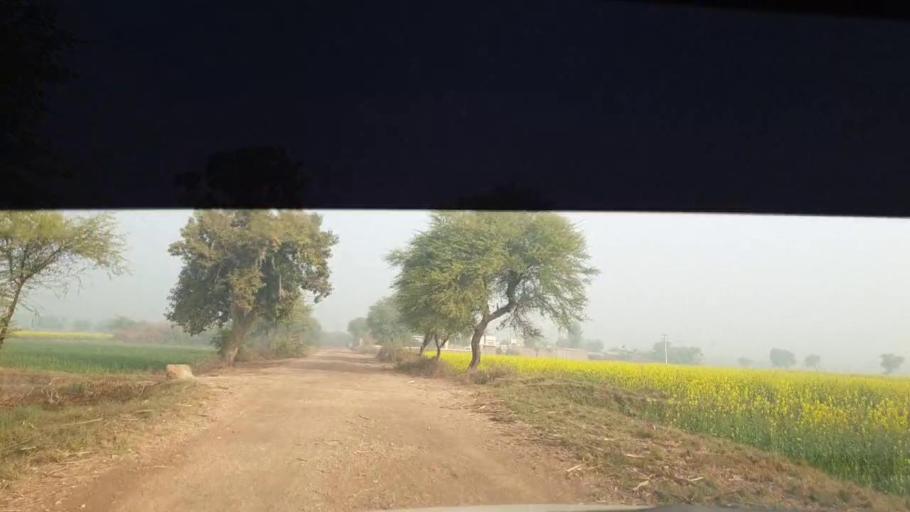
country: PK
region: Sindh
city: Berani
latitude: 25.7937
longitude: 68.7717
